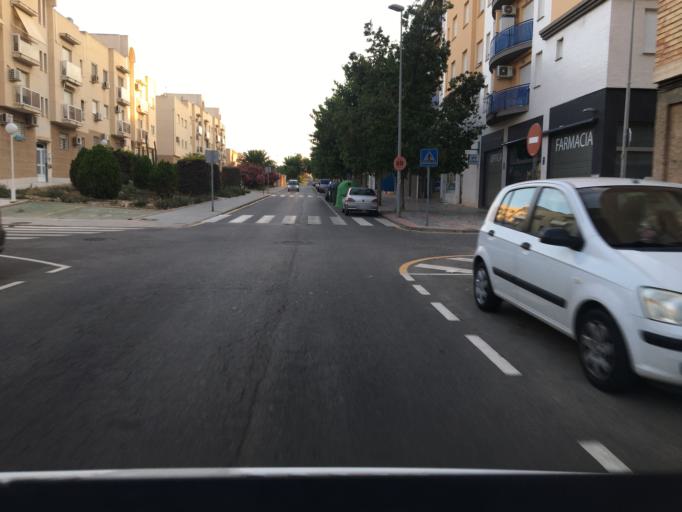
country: ES
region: Murcia
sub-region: Murcia
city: Cartagena
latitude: 37.6254
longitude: -0.9834
